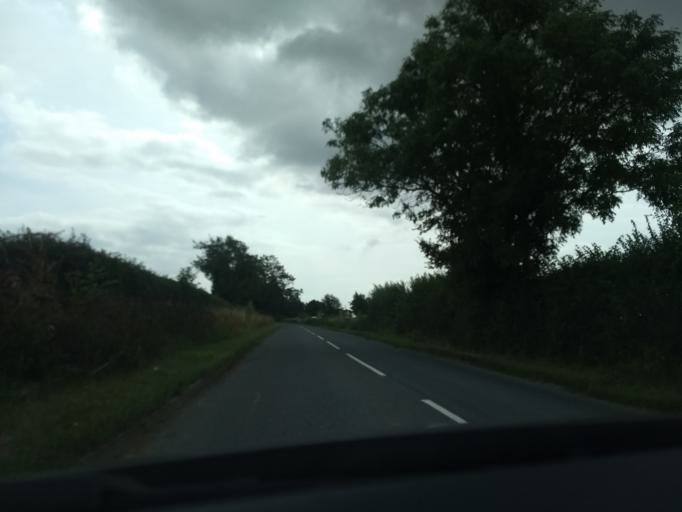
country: GB
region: England
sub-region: Suffolk
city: Ipswich
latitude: 51.9966
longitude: 1.1885
